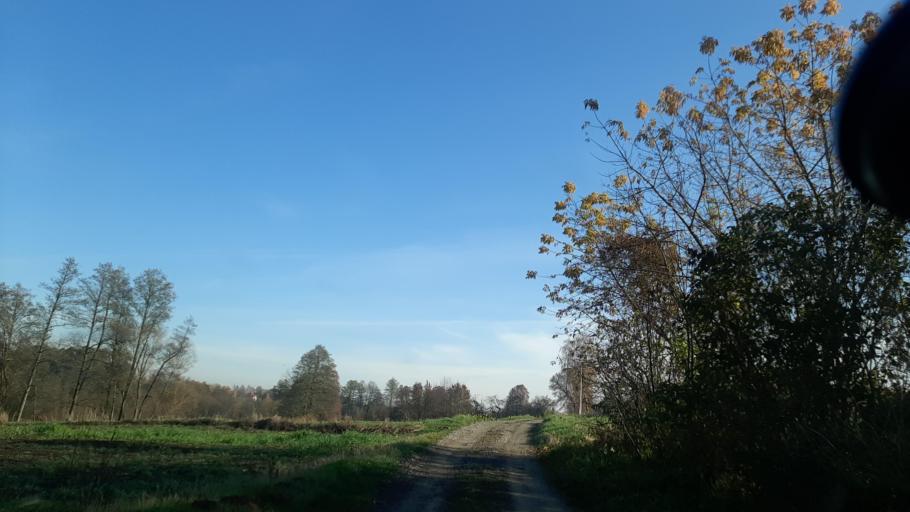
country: PL
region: Lublin Voivodeship
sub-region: Powiat lubelski
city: Lublin
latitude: 51.3114
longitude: 22.5209
